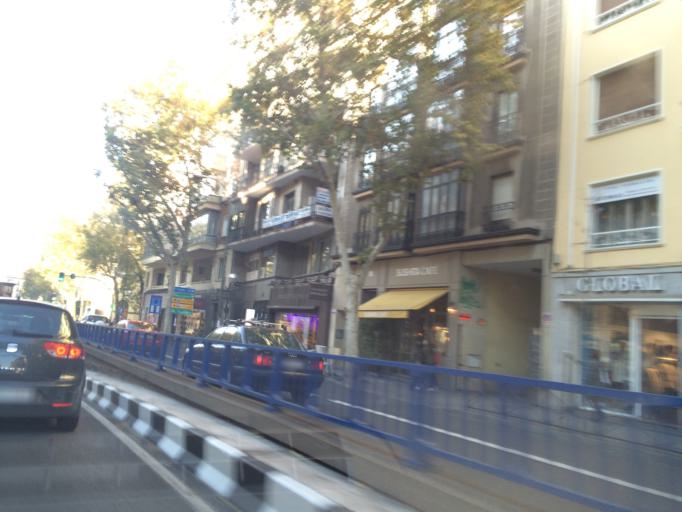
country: ES
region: Madrid
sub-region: Provincia de Madrid
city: Chamberi
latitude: 40.4303
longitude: -3.7124
